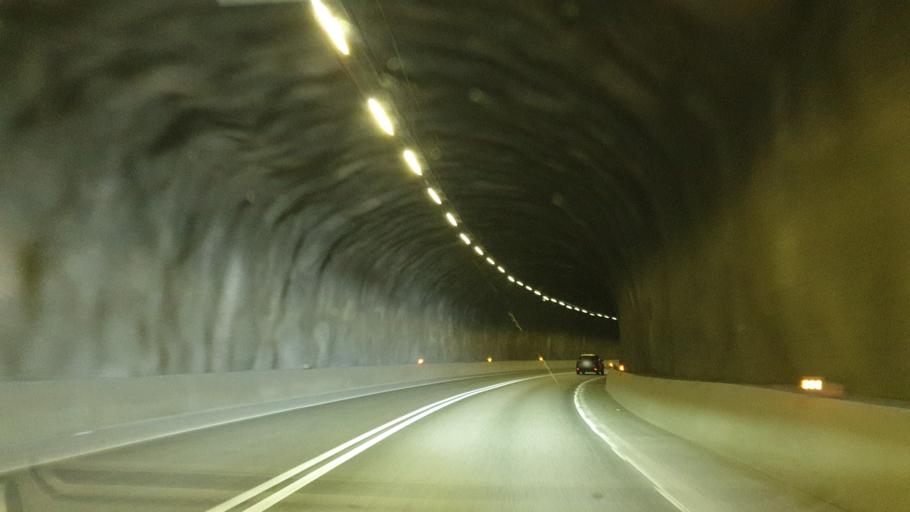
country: SE
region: Stockholm
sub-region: Nacka Kommun
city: Nacka
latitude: 59.3134
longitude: 18.1503
